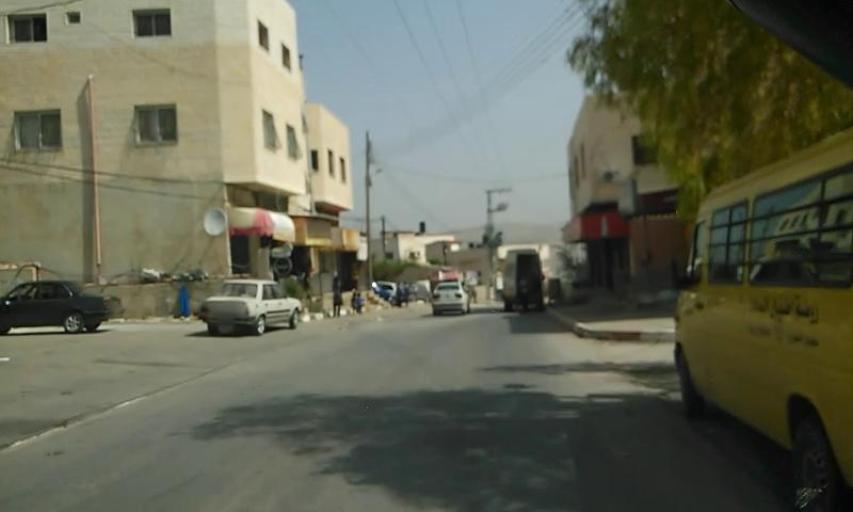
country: PS
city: Al Badhan
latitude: 32.2616
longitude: 35.3280
